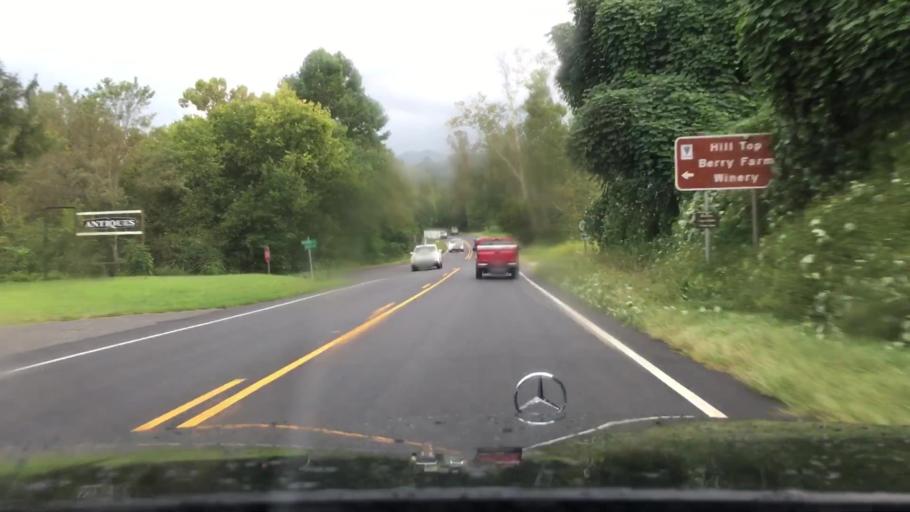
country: US
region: Virginia
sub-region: Nelson County
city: Nellysford
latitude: 37.9032
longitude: -78.8562
